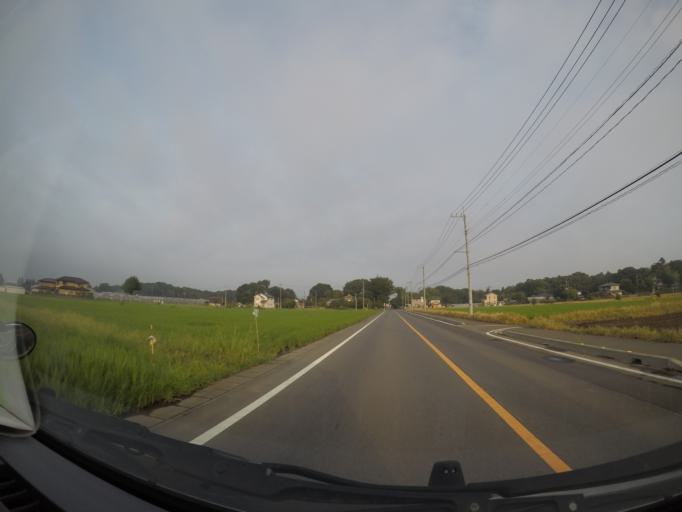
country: JP
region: Ibaraki
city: Koga
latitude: 36.2298
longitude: 139.7657
